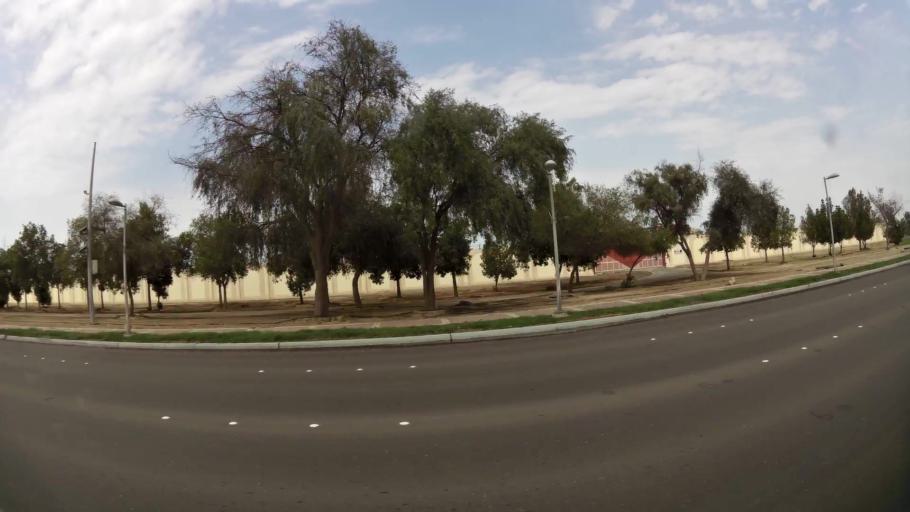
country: AE
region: Abu Dhabi
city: Abu Dhabi
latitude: 24.4174
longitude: 54.4727
